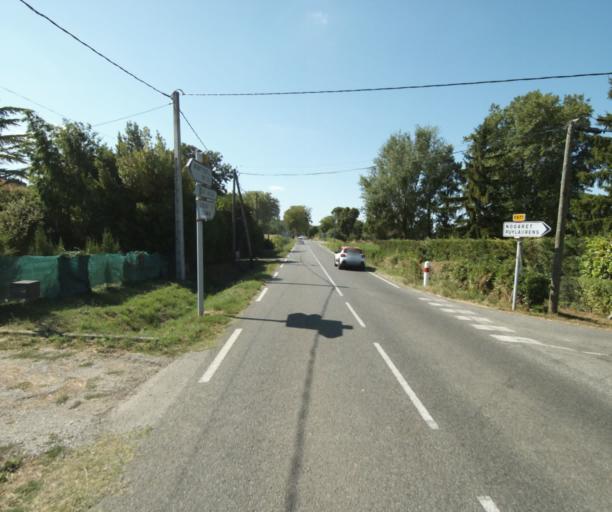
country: FR
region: Midi-Pyrenees
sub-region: Departement de la Haute-Garonne
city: Saint-Felix-Lauragais
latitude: 43.4883
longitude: 1.9068
